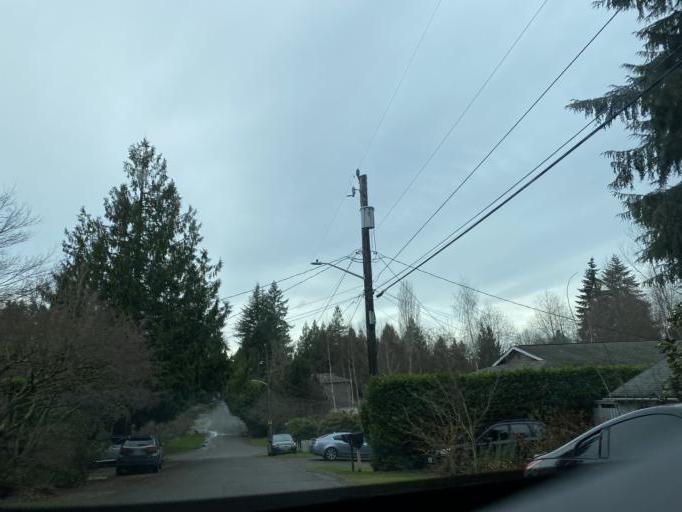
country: US
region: Washington
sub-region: King County
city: Lake Forest Park
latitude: 47.6966
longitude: -122.2979
